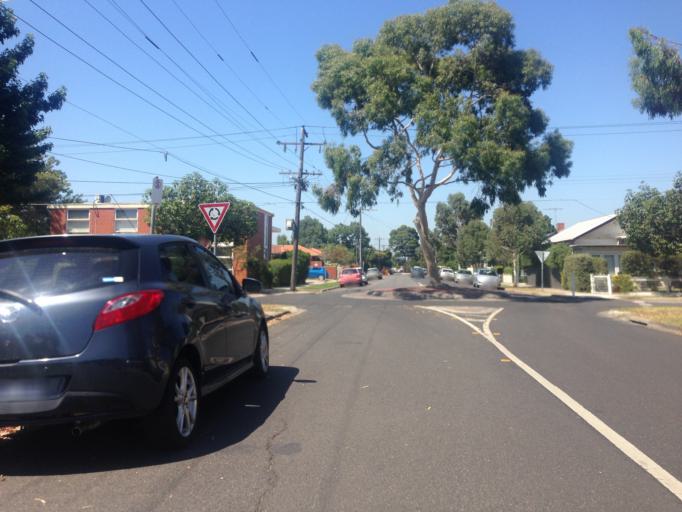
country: AU
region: Victoria
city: Thornbury
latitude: -37.7530
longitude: 144.9924
